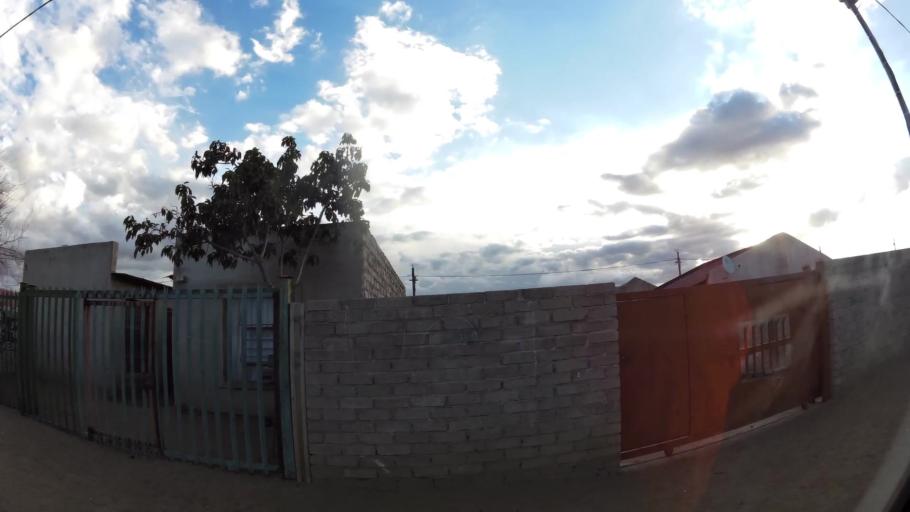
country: ZA
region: Limpopo
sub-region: Capricorn District Municipality
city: Polokwane
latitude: -23.9138
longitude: 29.4265
